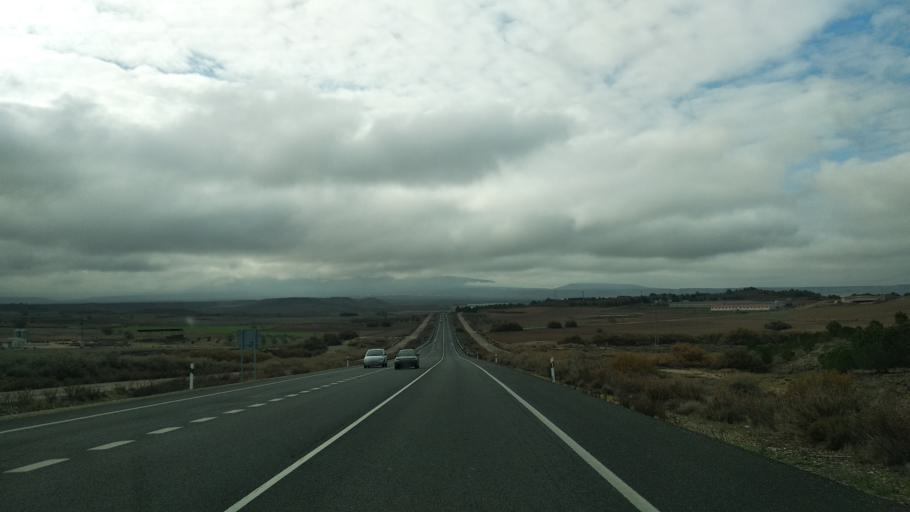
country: ES
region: La Rioja
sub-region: Provincia de La Rioja
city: Pradejon
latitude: 42.3210
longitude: -2.0231
